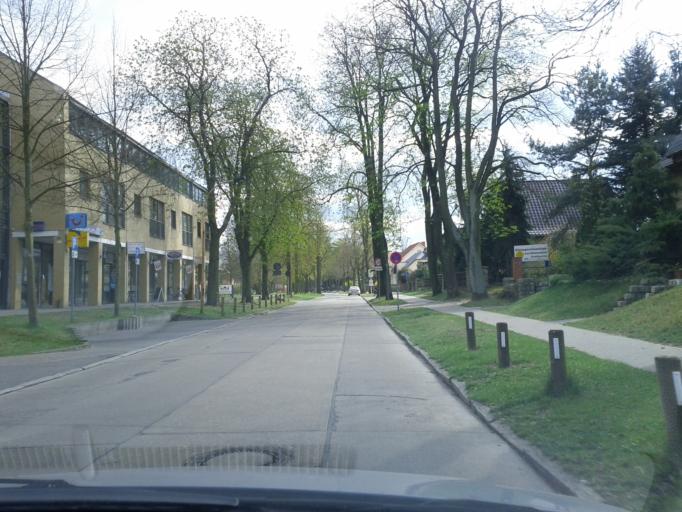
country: DE
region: Brandenburg
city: Schoneiche
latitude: 52.4770
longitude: 13.6994
